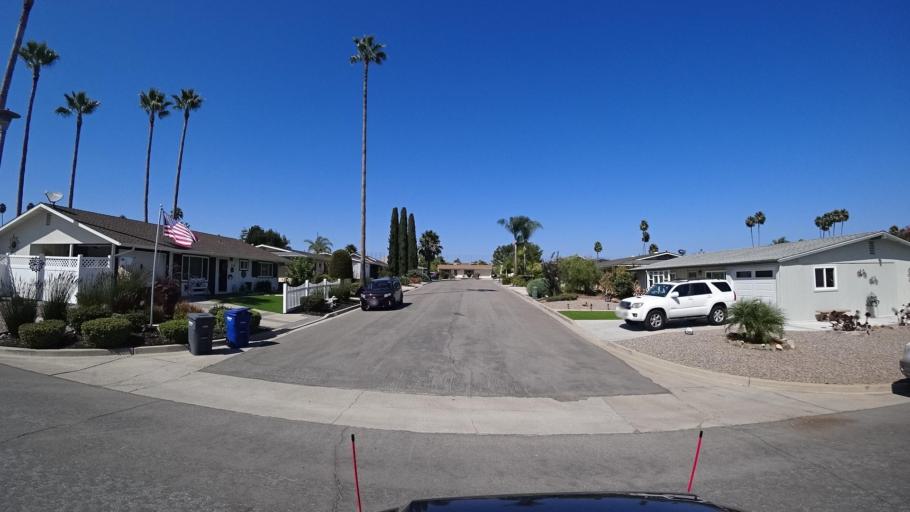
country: US
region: California
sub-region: San Diego County
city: Lake San Marcos
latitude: 33.1262
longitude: -117.2063
